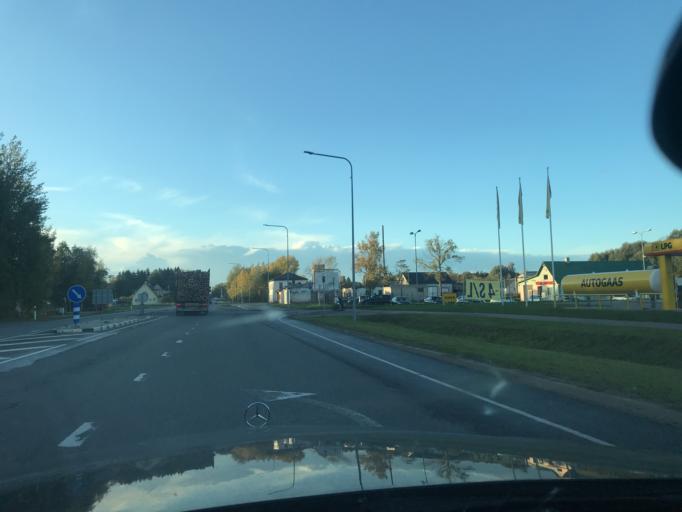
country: EE
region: Vorumaa
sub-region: Voru linn
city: Voru
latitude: 57.8580
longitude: 26.9752
